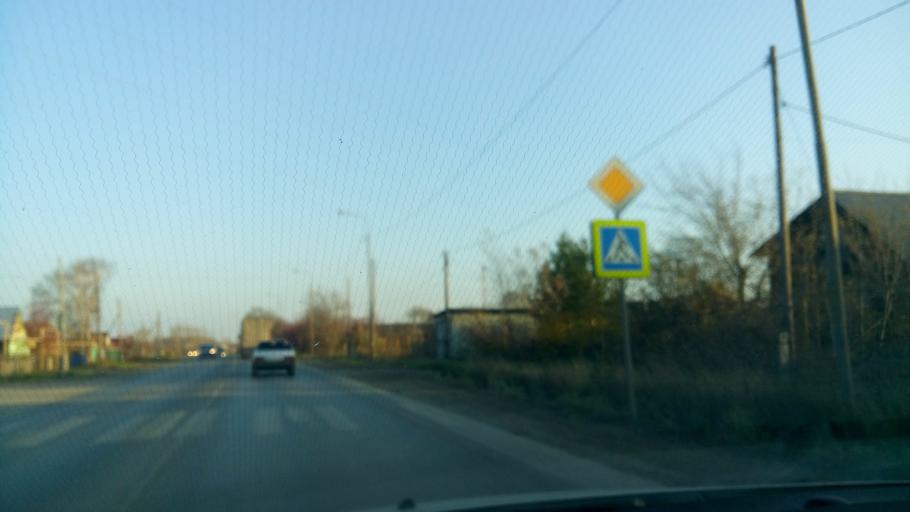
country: RU
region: Sverdlovsk
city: Bogdanovich
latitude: 56.7585
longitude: 62.0794
